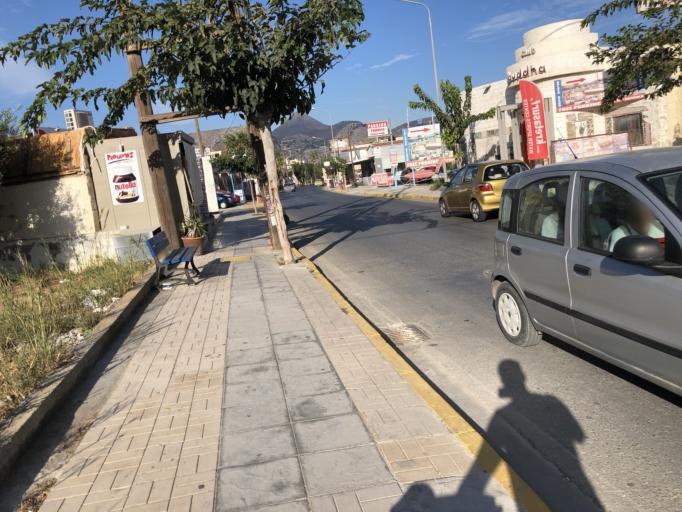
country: GR
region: Crete
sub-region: Nomos Irakleiou
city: Gazi
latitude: 35.3359
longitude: 25.0766
